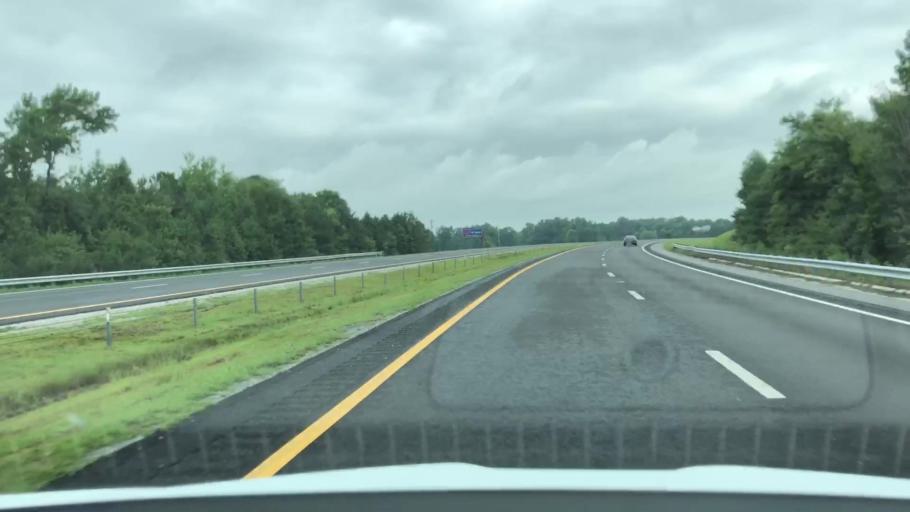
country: US
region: North Carolina
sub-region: Wayne County
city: Fremont
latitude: 35.5060
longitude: -77.9997
